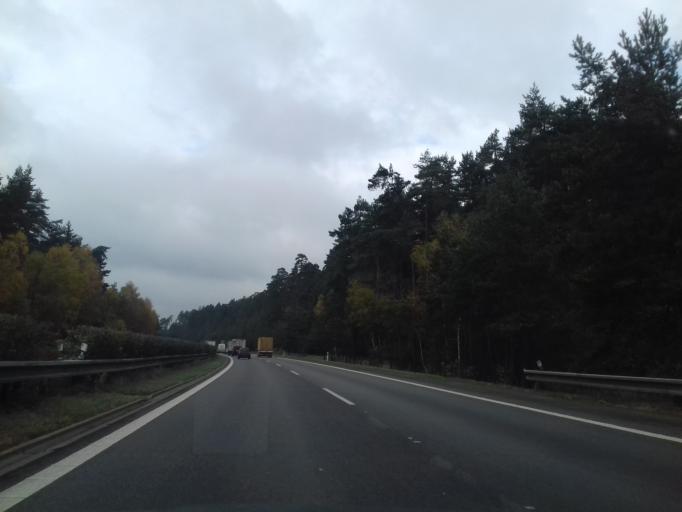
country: CZ
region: Central Bohemia
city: Zruc nad Sazavou
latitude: 49.6845
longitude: 15.1104
